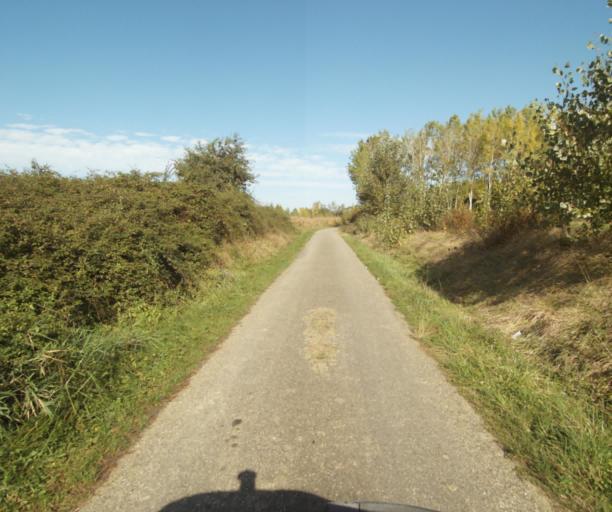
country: FR
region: Midi-Pyrenees
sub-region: Departement du Tarn-et-Garonne
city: Finhan
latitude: 43.9097
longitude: 1.2147
